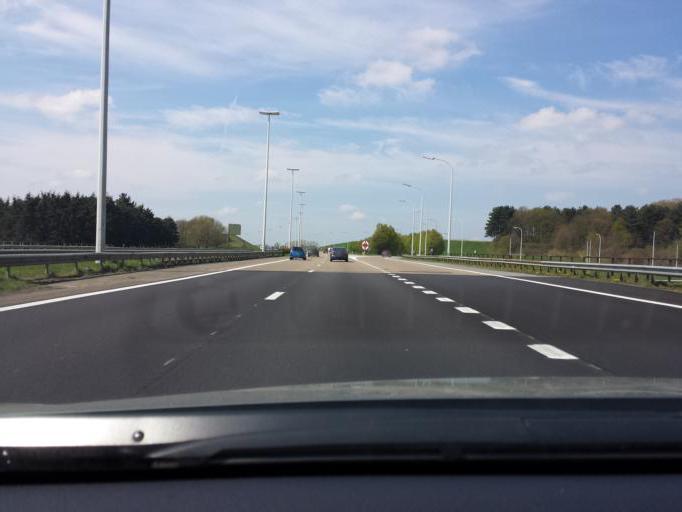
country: BE
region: Flanders
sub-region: Provincie Vlaams-Brabant
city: Bekkevoort
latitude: 50.9526
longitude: 5.0003
